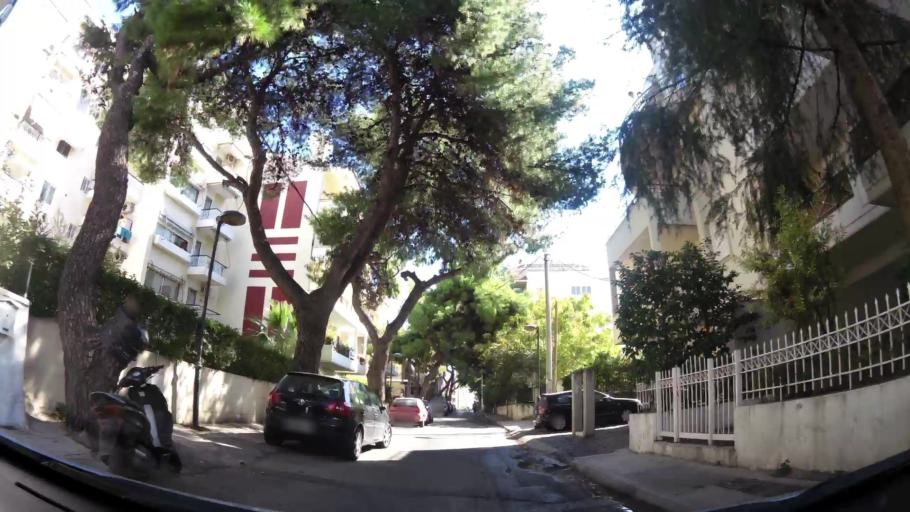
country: GR
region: Attica
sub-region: Nomarchia Athinas
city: Metamorfosi
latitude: 38.0617
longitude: 23.7662
